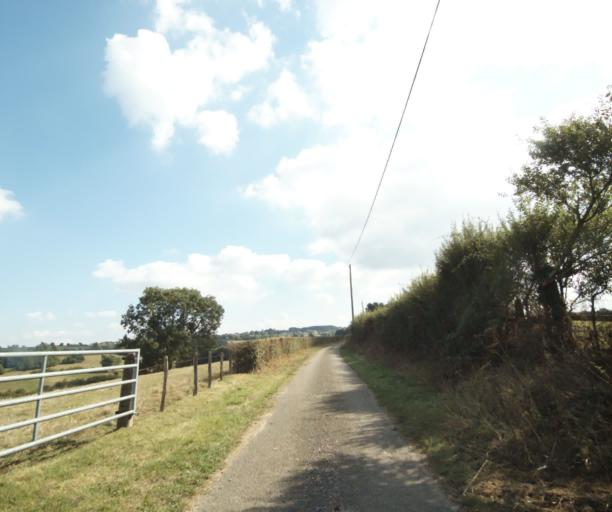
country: FR
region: Bourgogne
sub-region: Departement de Saone-et-Loire
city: Charolles
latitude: 46.3561
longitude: 4.2432
